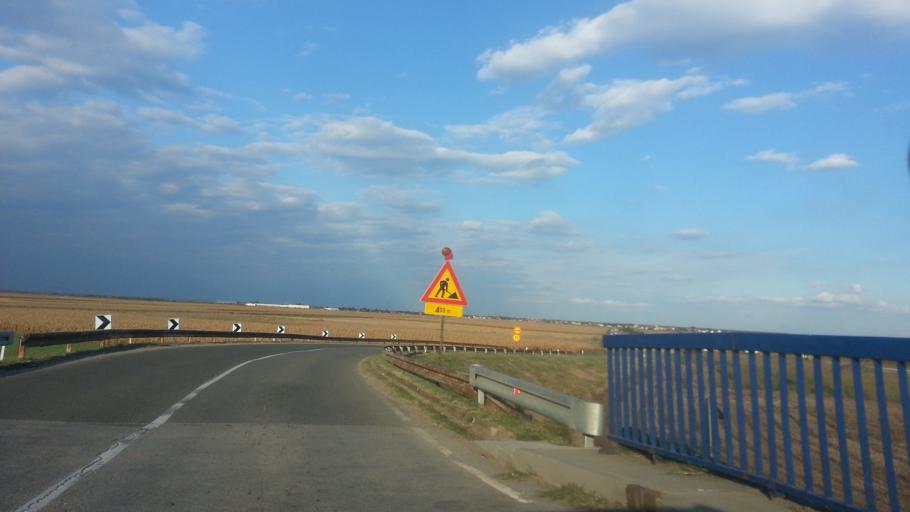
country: RS
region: Autonomna Pokrajina Vojvodina
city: Nova Pazova
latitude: 44.9679
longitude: 20.2382
